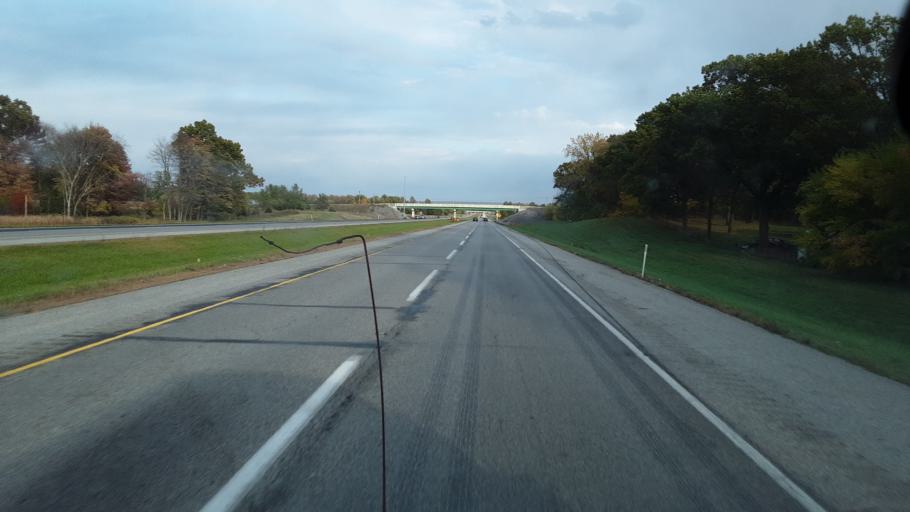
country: US
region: Michigan
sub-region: Saint Joseph County
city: White Pigeon
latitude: 41.7518
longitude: -85.6065
